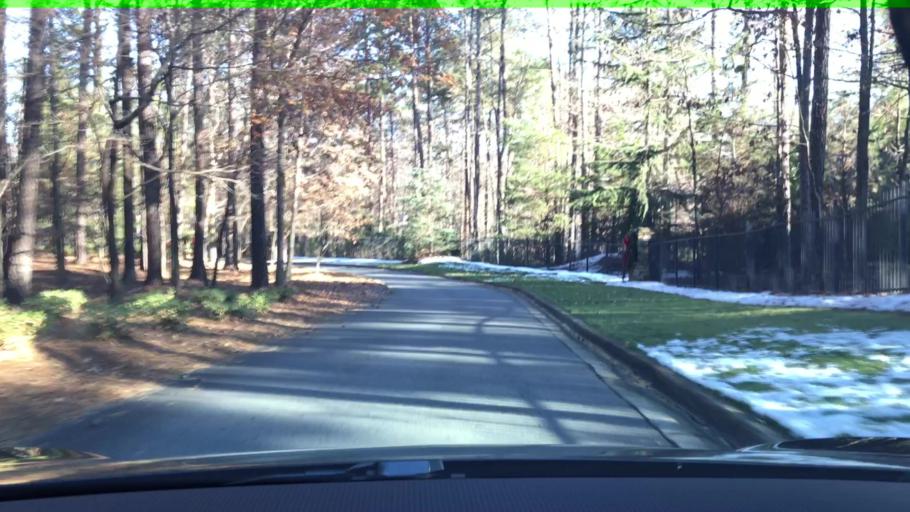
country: US
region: Georgia
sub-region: Gwinnett County
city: Suwanee
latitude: 34.0694
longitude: -84.0913
